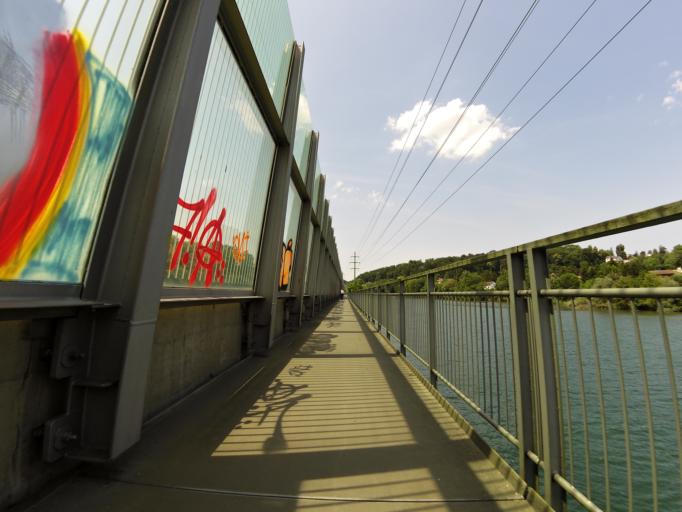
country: CH
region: Aargau
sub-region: Bezirk Baden
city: Wurenlos
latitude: 47.4321
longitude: 8.3609
